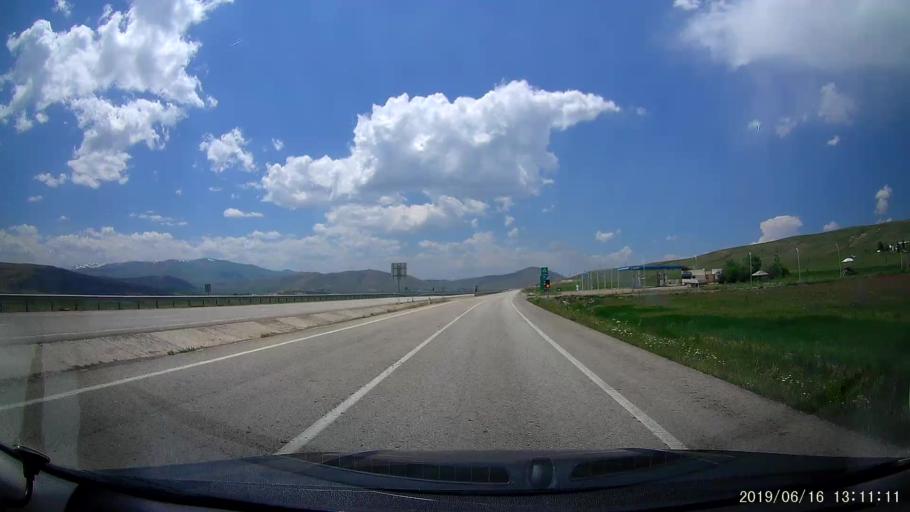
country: TR
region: Agri
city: Diyadin
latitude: 39.5910
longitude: 43.6143
